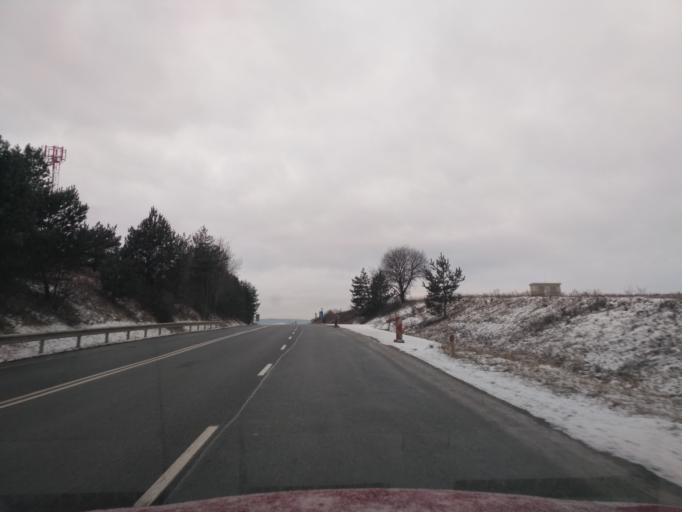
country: SK
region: Presovsky
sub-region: Okres Presov
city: Presov
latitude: 49.0004
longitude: 21.1964
